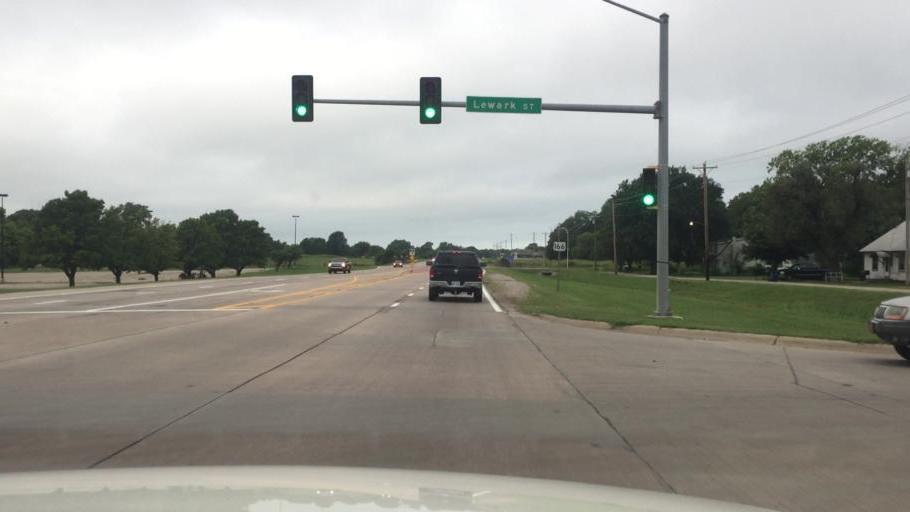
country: US
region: Kansas
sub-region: Montgomery County
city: Coffeyville
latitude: 37.0334
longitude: -95.6444
